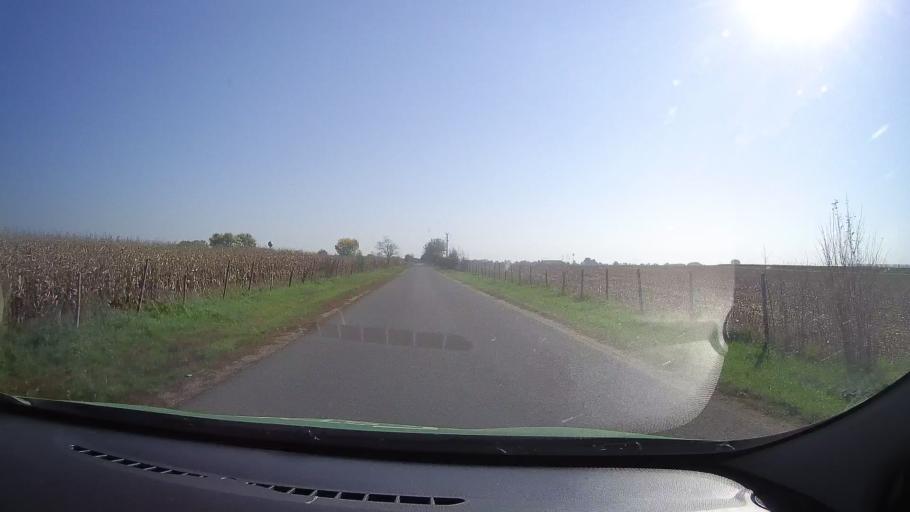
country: RO
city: Foieni
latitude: 47.6970
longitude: 22.3617
